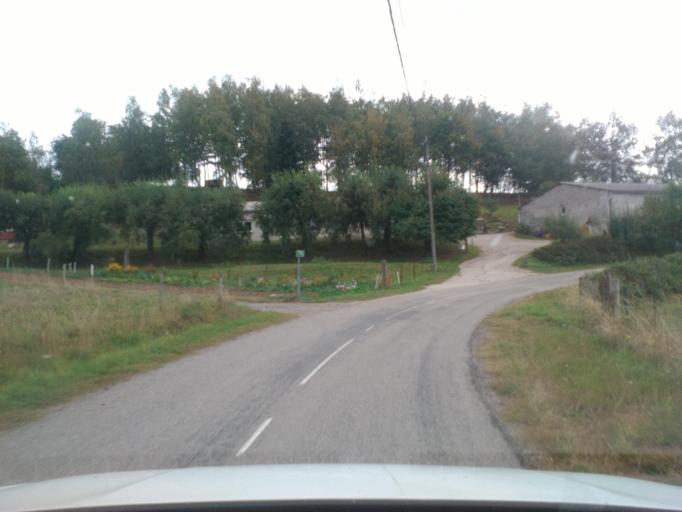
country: FR
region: Lorraine
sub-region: Departement des Vosges
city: Senones
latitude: 48.3750
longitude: 7.0014
